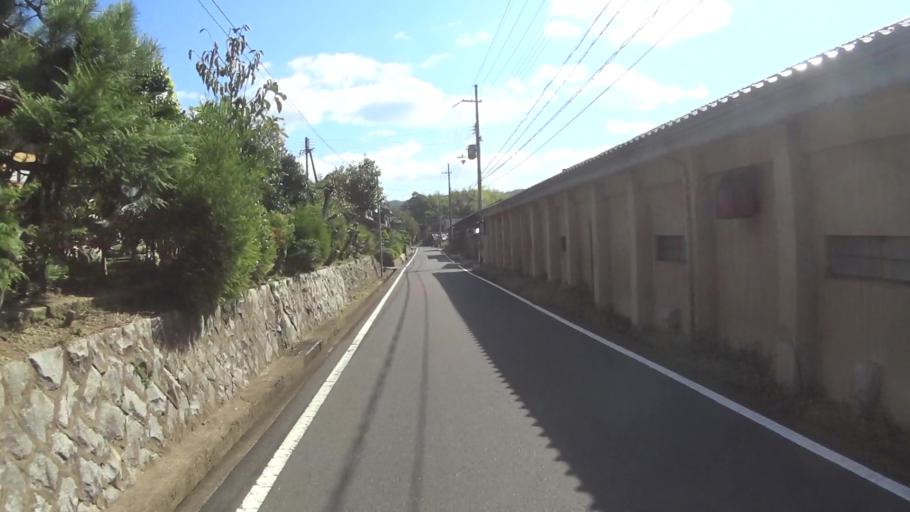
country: JP
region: Kyoto
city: Miyazu
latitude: 35.7079
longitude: 135.0880
